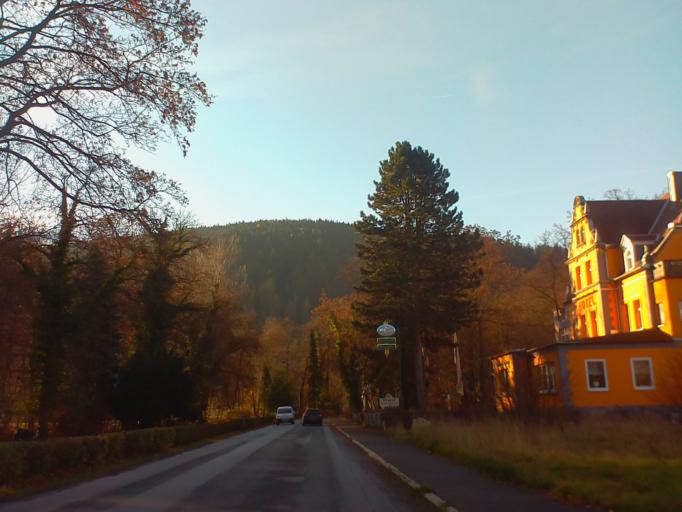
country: DE
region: Thuringia
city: Bad Blankenburg
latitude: 50.6771
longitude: 11.2701
